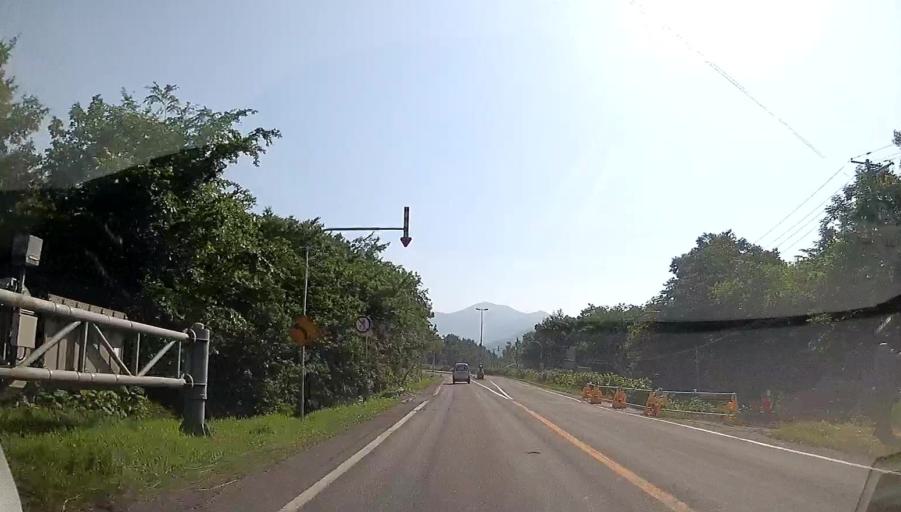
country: JP
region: Hokkaido
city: Otofuke
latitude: 42.9890
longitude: 142.8415
